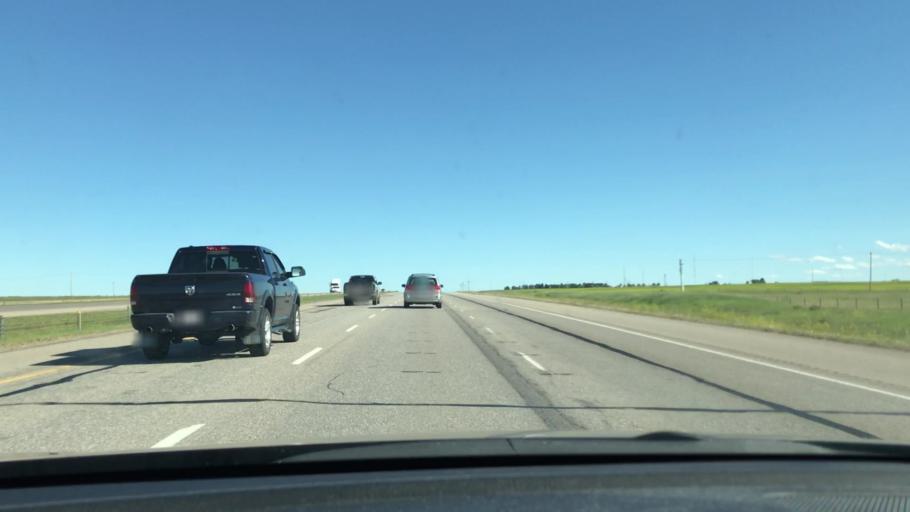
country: CA
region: Alberta
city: Crossfield
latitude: 51.4476
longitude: -114.0128
